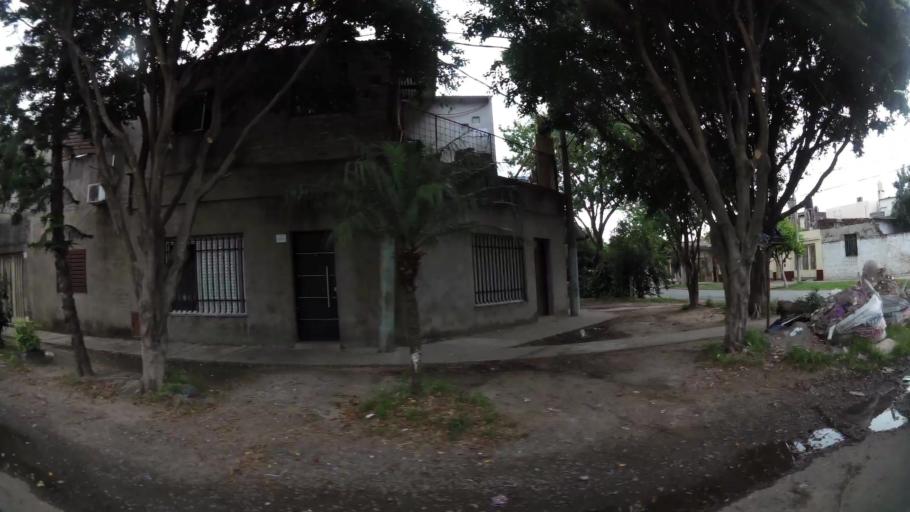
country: AR
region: Santa Fe
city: Gobernador Galvez
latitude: -32.9966
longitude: -60.6680
